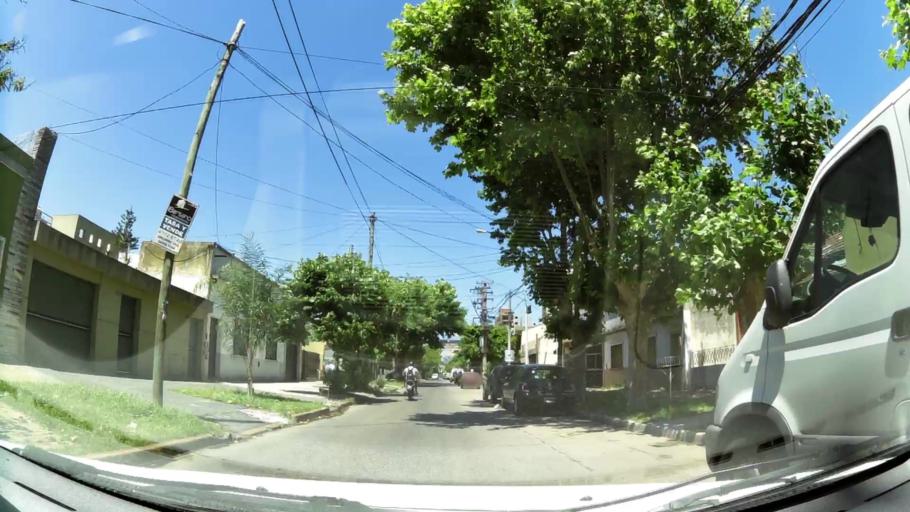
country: AR
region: Buenos Aires
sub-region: Partido de General San Martin
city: General San Martin
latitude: -34.5995
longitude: -58.5273
